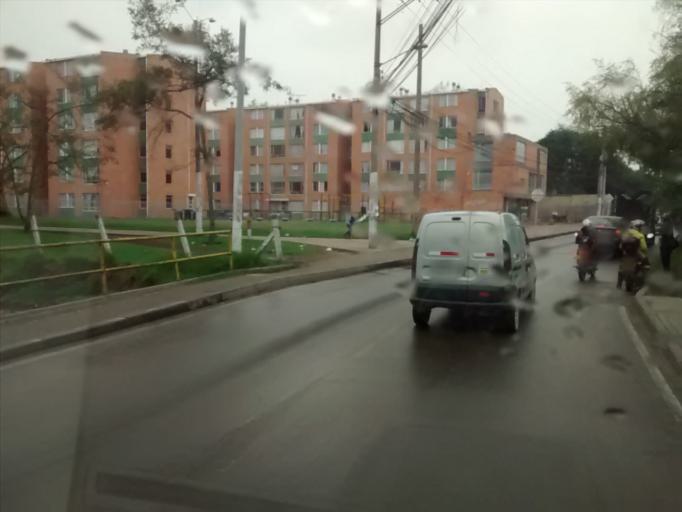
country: CO
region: Cundinamarca
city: Cota
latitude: 4.7580
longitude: -74.0920
